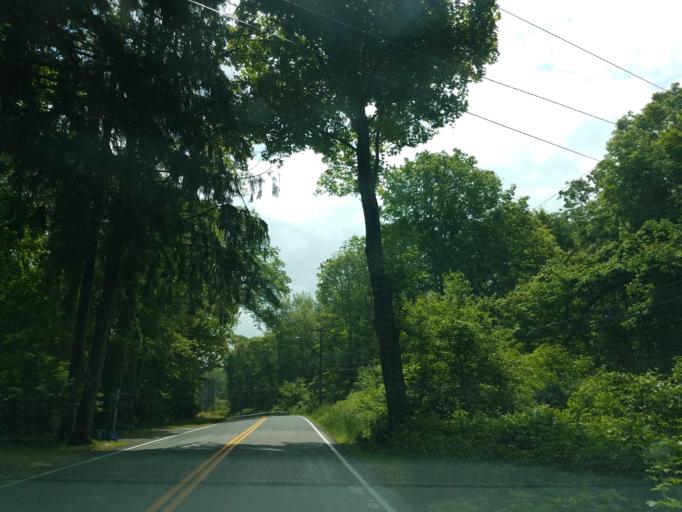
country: US
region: Connecticut
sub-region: New London County
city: Old Mystic
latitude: 41.3730
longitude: -71.9110
